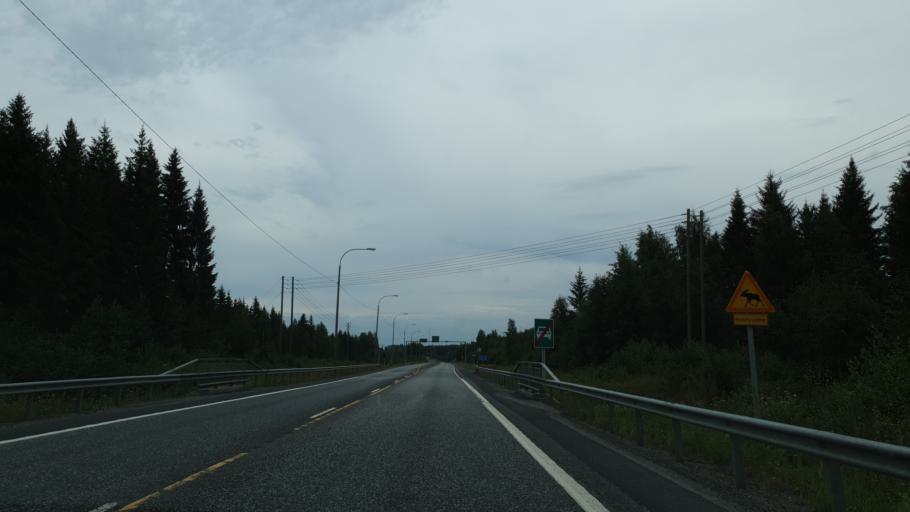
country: FI
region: North Karelia
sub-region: Joensuu
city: Pyhaeselkae
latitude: 62.5157
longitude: 29.8891
